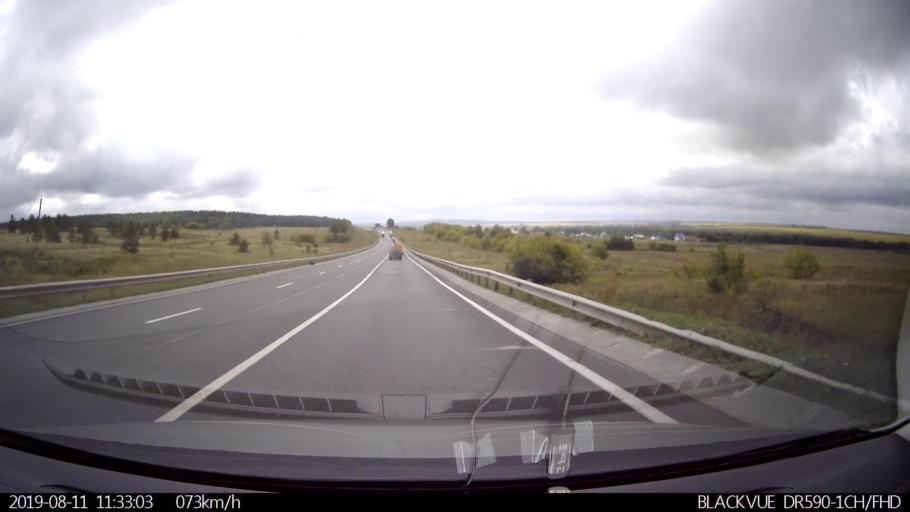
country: RU
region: Ulyanovsk
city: Krasnyy Gulyay
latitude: 54.0313
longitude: 48.2126
